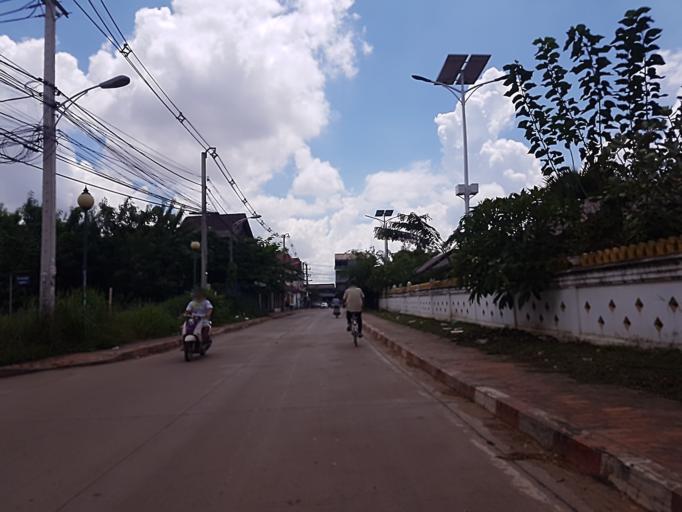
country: LA
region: Vientiane
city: Vientiane
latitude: 17.9767
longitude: 102.6374
